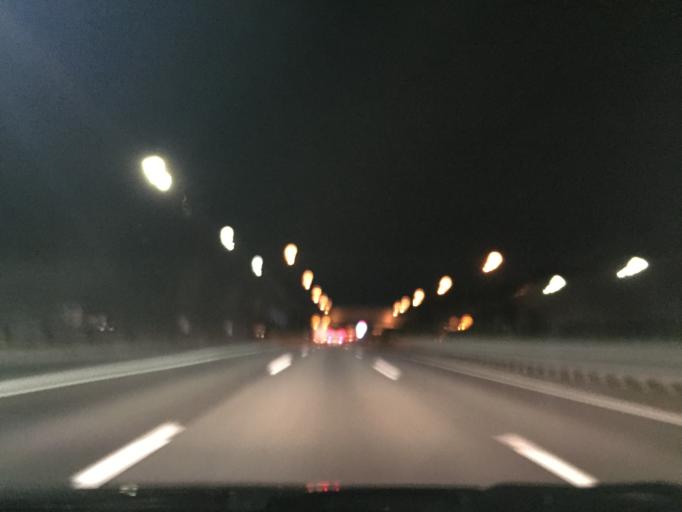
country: JP
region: Kanagawa
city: Isehara
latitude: 35.3896
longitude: 139.2799
